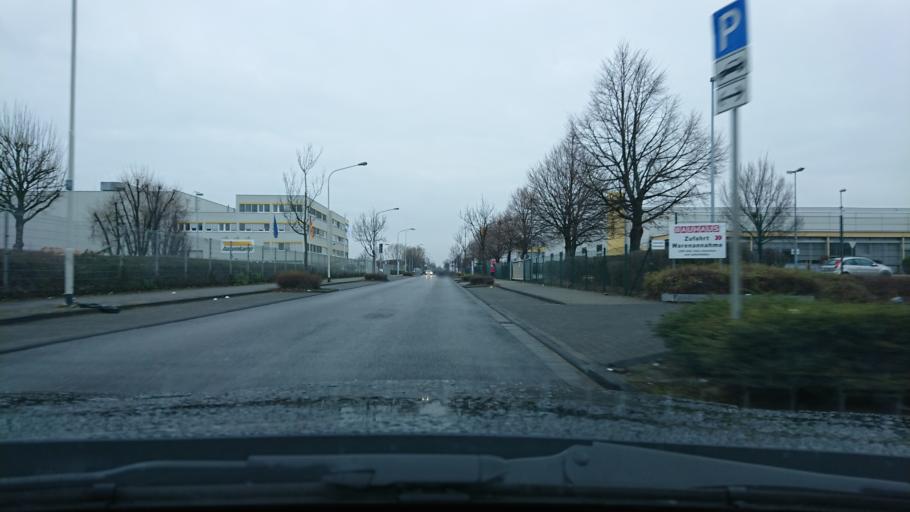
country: DE
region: North Rhine-Westphalia
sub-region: Regierungsbezirk Koln
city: Frechen
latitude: 50.9197
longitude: 6.8364
